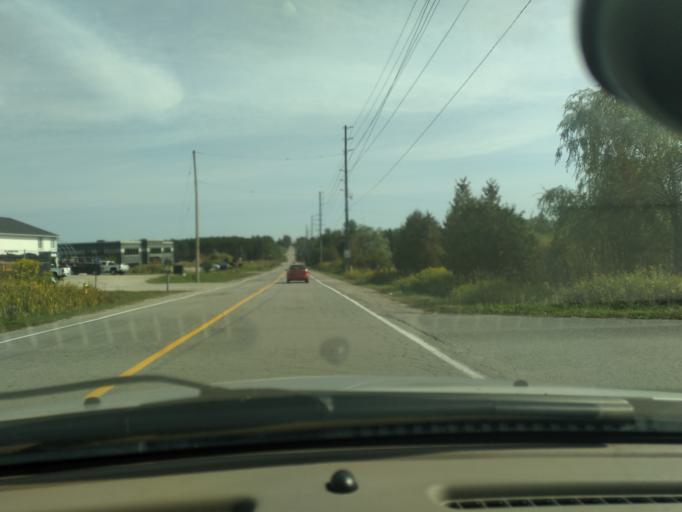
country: CA
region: Ontario
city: Innisfil
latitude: 44.3276
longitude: -79.6640
